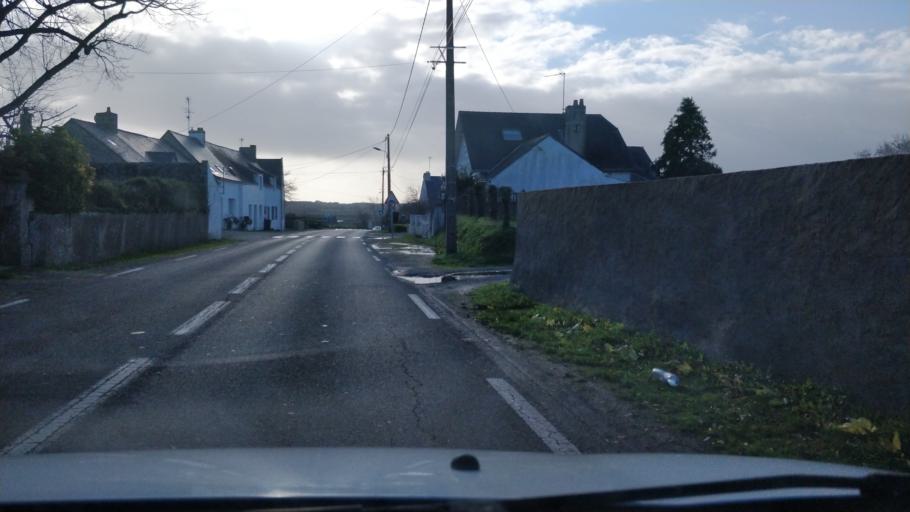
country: FR
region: Pays de la Loire
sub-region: Departement de la Loire-Atlantique
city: Asserac
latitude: 47.4140
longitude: -2.3993
